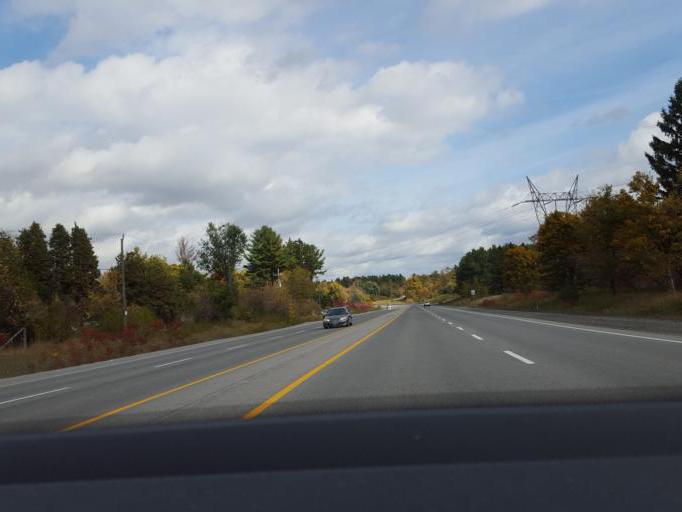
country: CA
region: Ontario
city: Pickering
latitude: 43.8805
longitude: -79.1055
